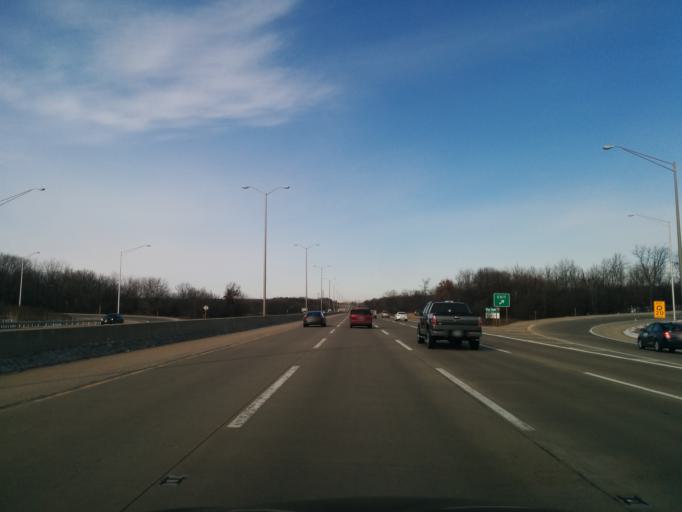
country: US
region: Illinois
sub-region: Lake County
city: Gurnee
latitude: 42.3457
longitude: -87.9236
